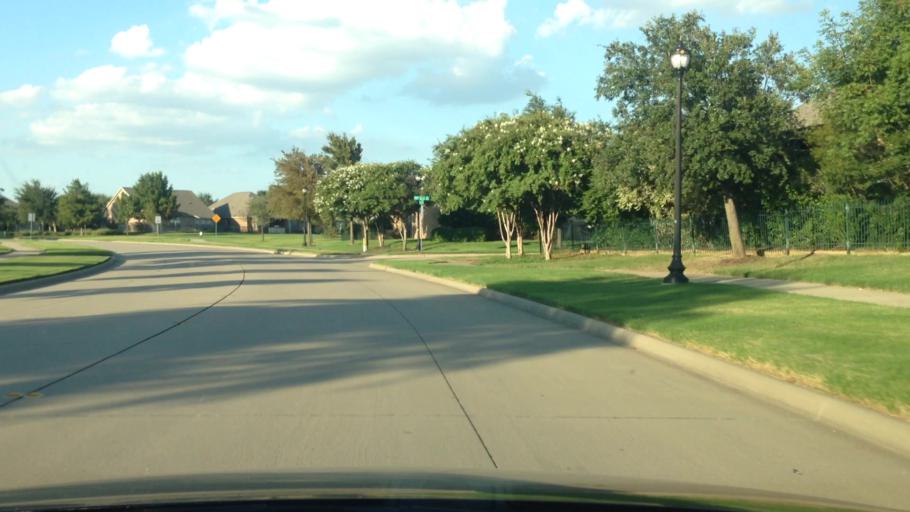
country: US
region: Texas
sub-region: Denton County
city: Little Elm
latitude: 33.1400
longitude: -96.8972
